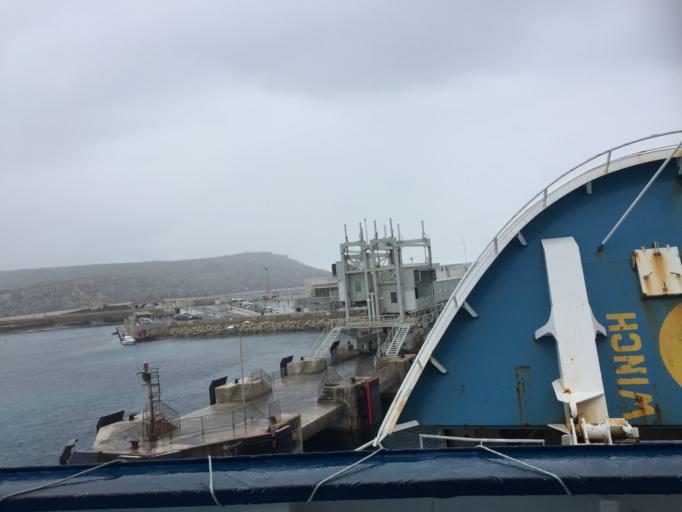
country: MT
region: Il-Mellieha
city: Mellieha
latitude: 35.9898
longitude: 14.3300
